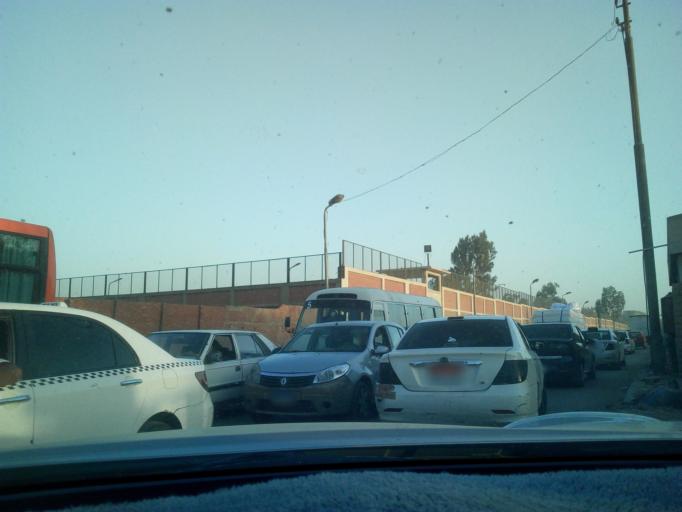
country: EG
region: Muhafazat al Qalyubiyah
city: Al Khankah
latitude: 30.1268
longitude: 31.3552
